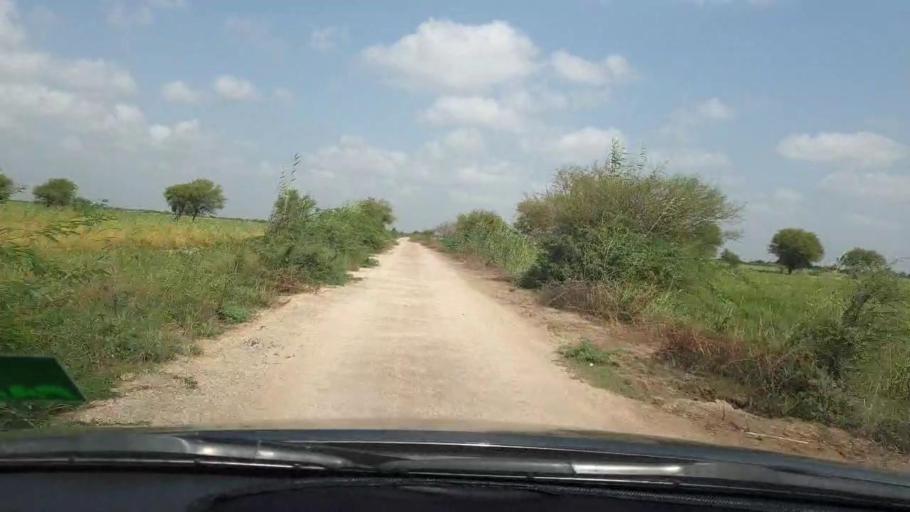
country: PK
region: Sindh
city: Tando Bago
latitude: 24.8652
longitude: 69.0355
